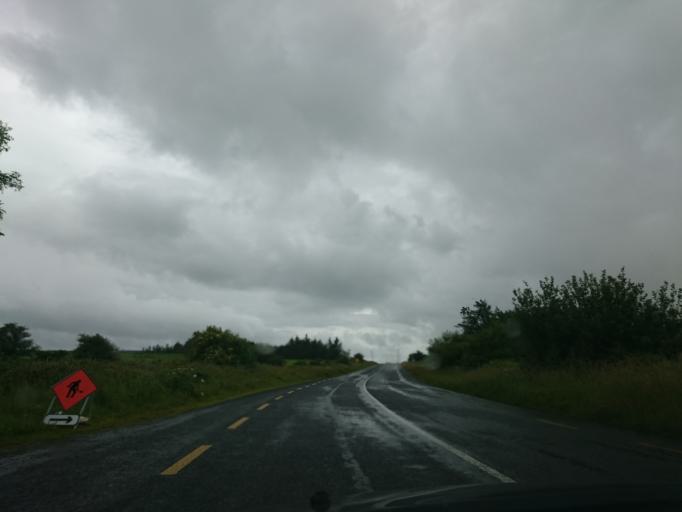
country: IE
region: Connaught
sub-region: Maigh Eo
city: Ballina
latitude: 54.1957
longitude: -9.2023
